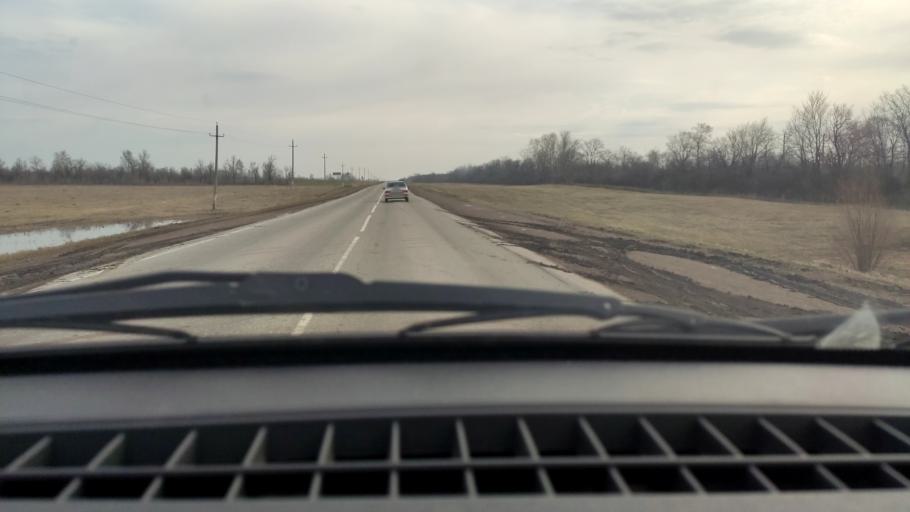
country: RU
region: Bashkortostan
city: Davlekanovo
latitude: 54.3020
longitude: 55.1337
